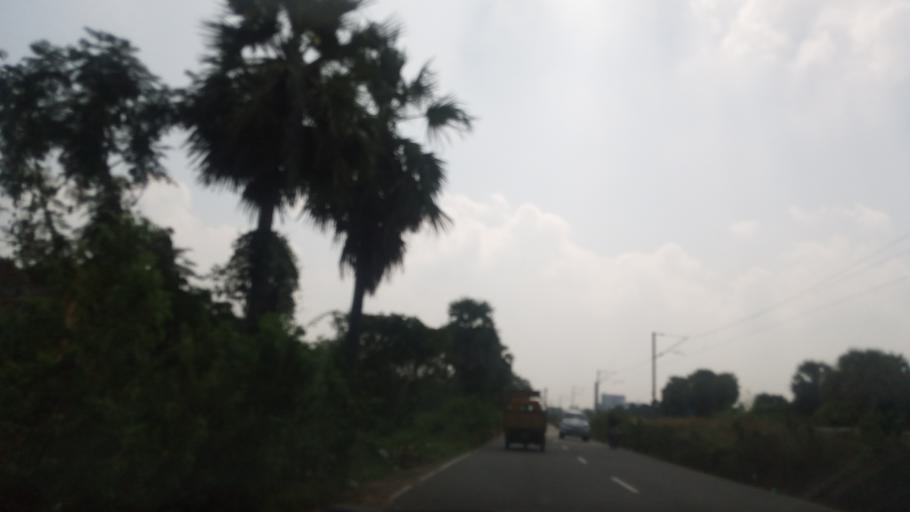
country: IN
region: Tamil Nadu
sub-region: Kancheepuram
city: Kanchipuram
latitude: 12.8827
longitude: 79.6886
